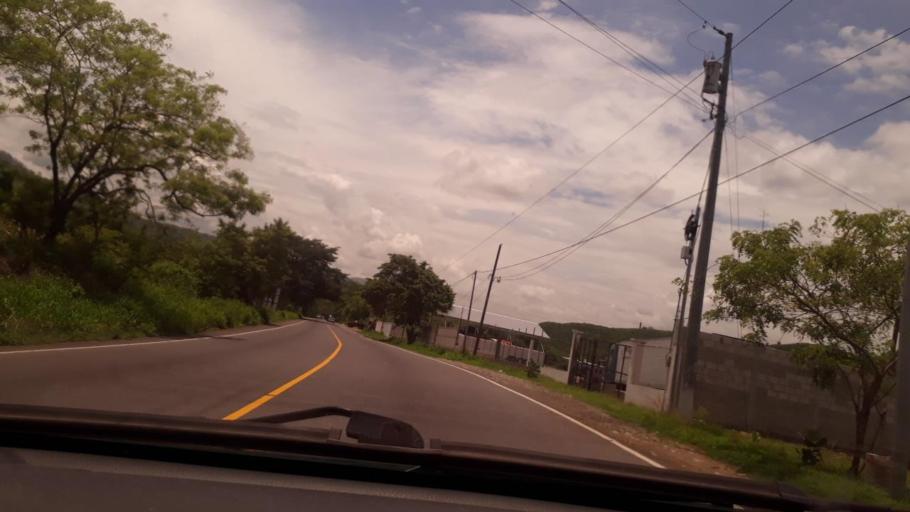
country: GT
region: Zacapa
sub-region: Municipio de Zacapa
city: Gualan
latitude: 15.1194
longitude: -89.3856
